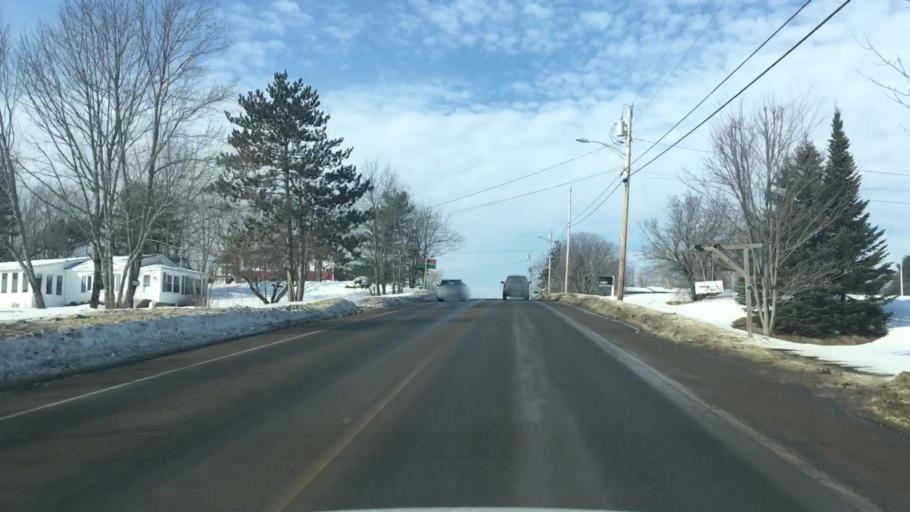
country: US
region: Maine
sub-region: Penobscot County
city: Hermon
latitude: 44.8449
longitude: -68.8673
